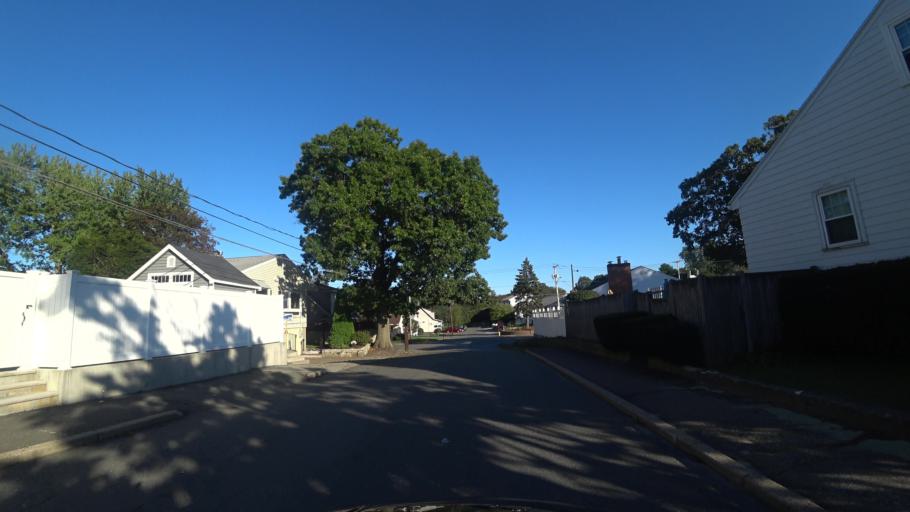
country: US
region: Massachusetts
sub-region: Middlesex County
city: Medford
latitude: 42.4373
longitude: -71.0899
